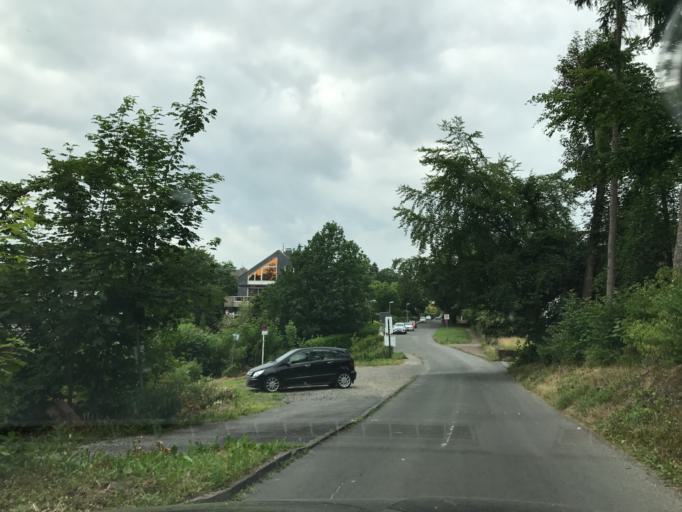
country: DE
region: North Rhine-Westphalia
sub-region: Regierungsbezirk Dusseldorf
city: Essen
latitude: 51.3959
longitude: 6.9888
